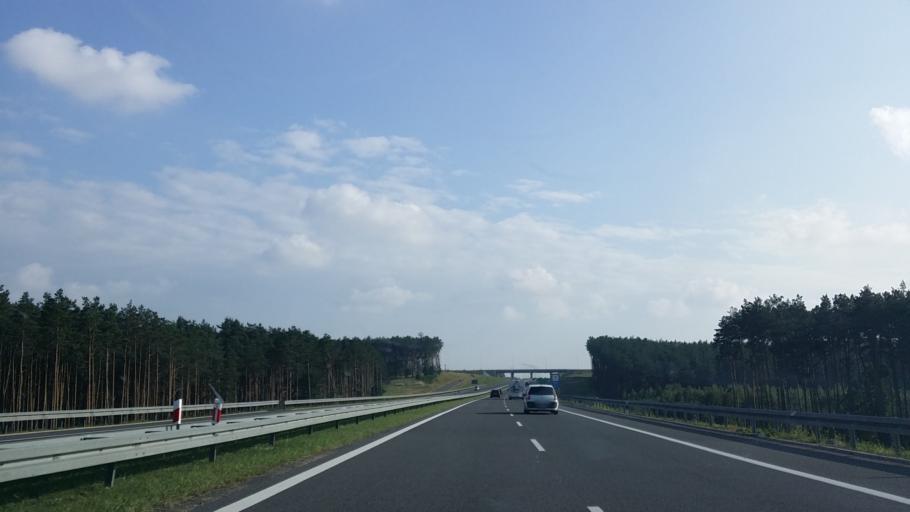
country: PL
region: Lubusz
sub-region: Powiat swiebodzinski
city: Swiebodzin
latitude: 52.3302
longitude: 15.5555
